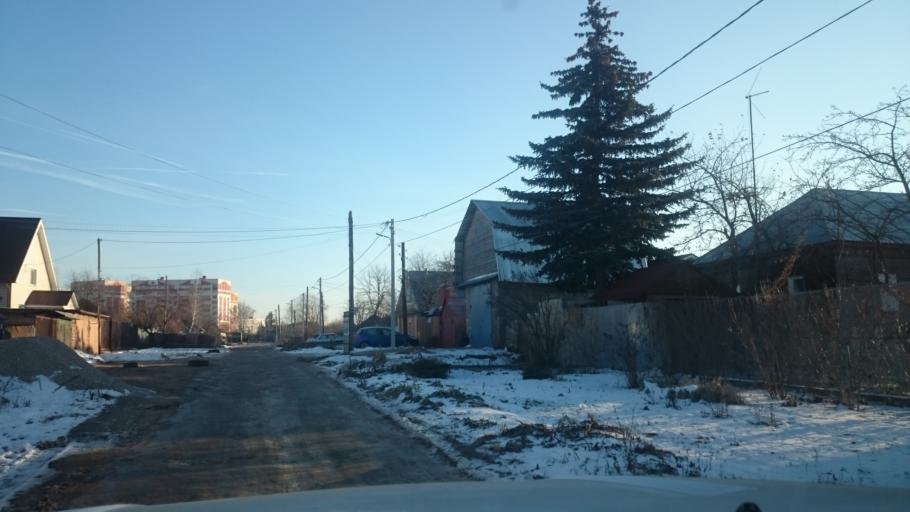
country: RU
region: Tula
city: Tula
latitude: 54.2015
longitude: 37.6916
